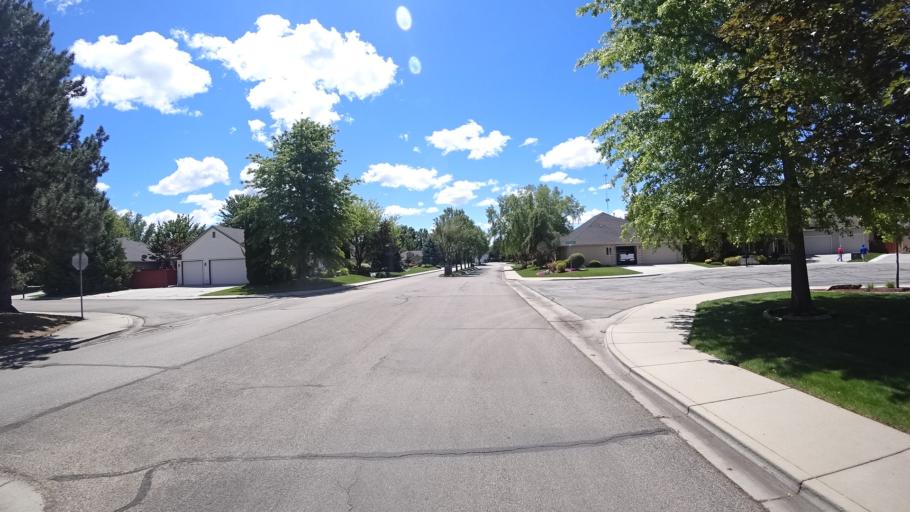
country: US
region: Idaho
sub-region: Ada County
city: Eagle
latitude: 43.6499
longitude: -116.3408
